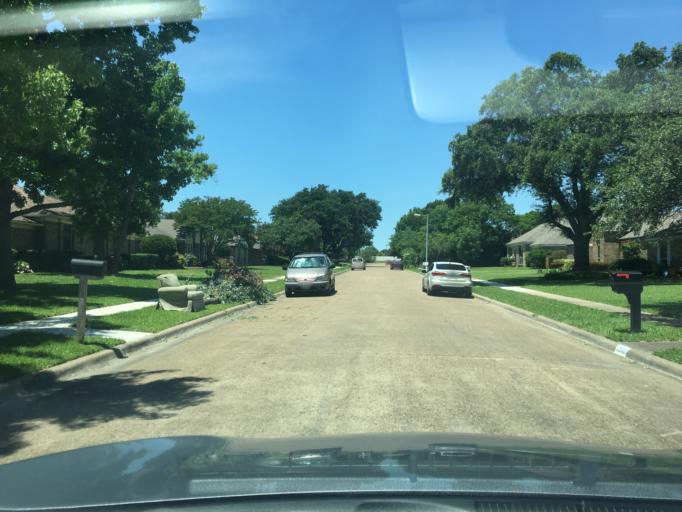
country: US
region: Texas
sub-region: Dallas County
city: Richardson
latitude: 32.9430
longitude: -96.6924
